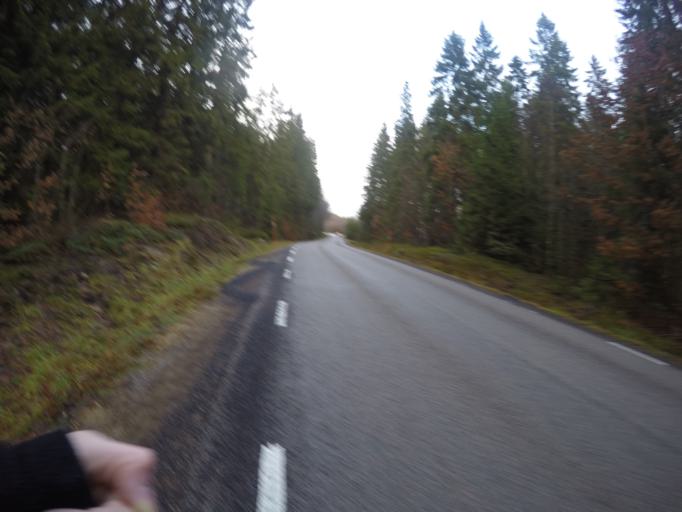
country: SE
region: Skane
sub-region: Osby Kommun
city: Lonsboda
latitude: 56.3764
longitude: 14.3447
